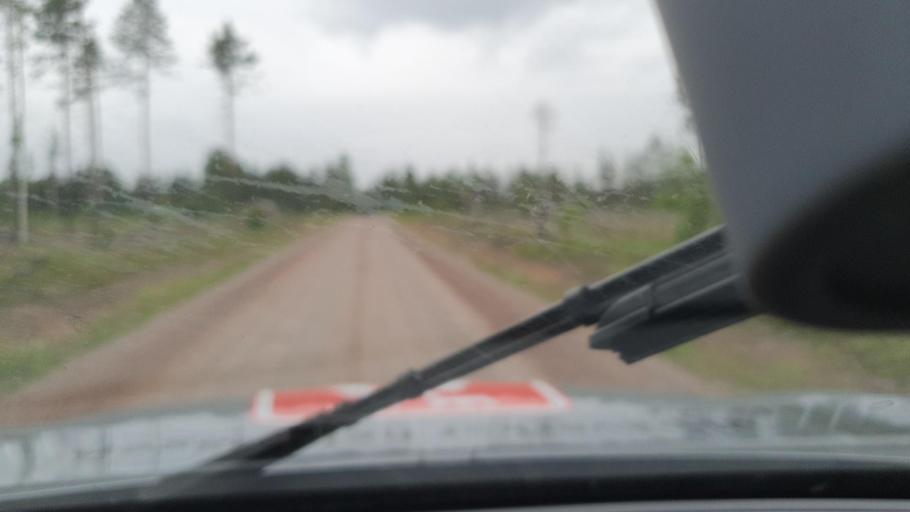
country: SE
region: Norrbotten
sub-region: Overkalix Kommun
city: OEverkalix
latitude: 66.4941
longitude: 22.7631
